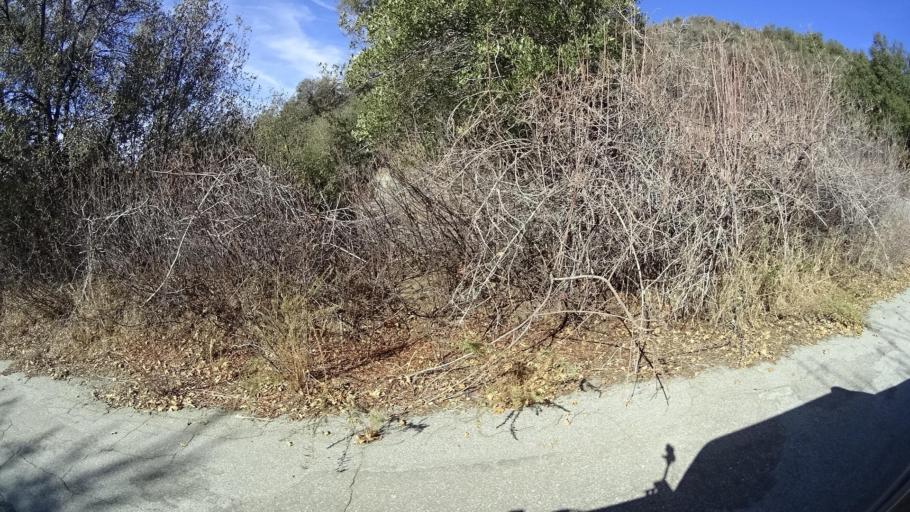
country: US
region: California
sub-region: Kern County
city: Bodfish
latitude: 35.4662
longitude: -118.6481
